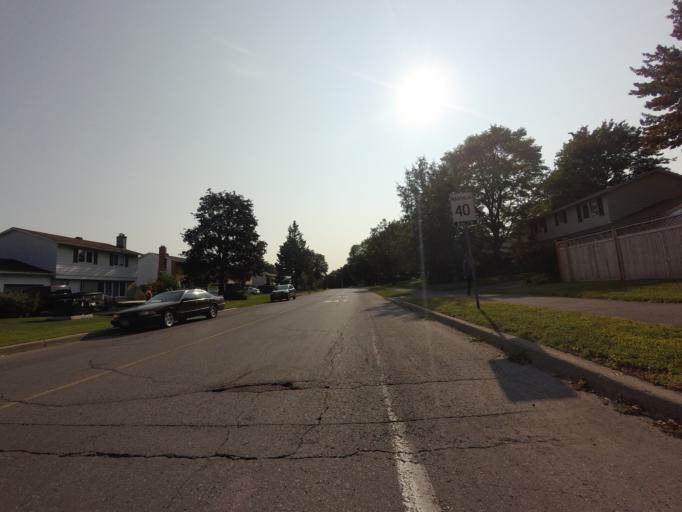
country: CA
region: Ontario
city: Bells Corners
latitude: 45.2996
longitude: -75.8775
